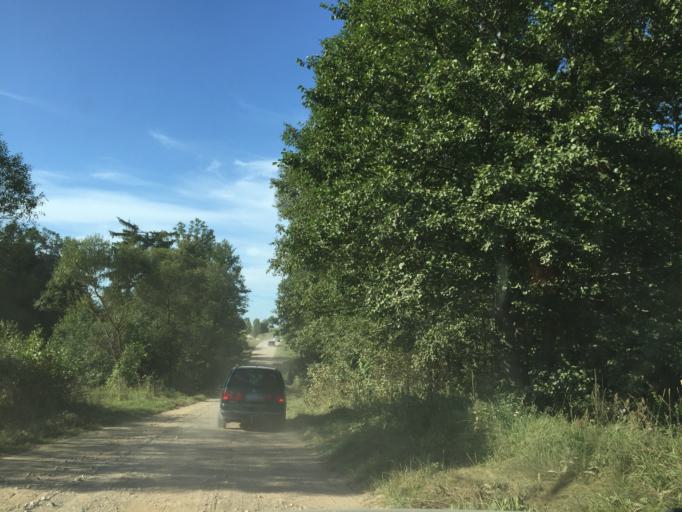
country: LT
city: Zarasai
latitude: 55.7944
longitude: 25.9526
